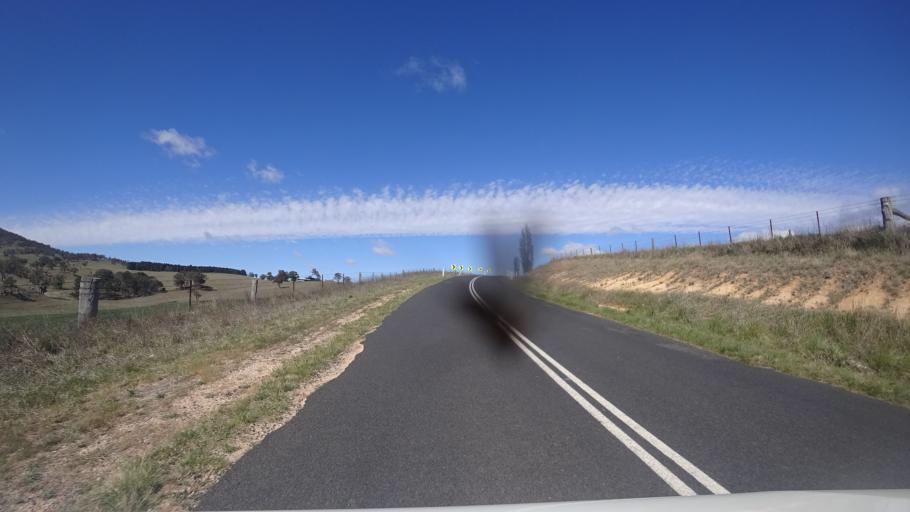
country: AU
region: New South Wales
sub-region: Lithgow
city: Portland
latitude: -33.5186
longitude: 149.9518
